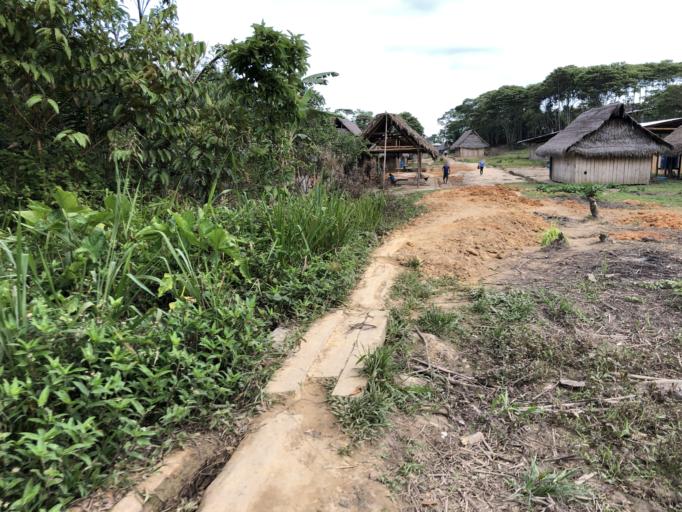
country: PE
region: Loreto
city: Puerto Galilea
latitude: -4.0570
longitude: -77.7608
